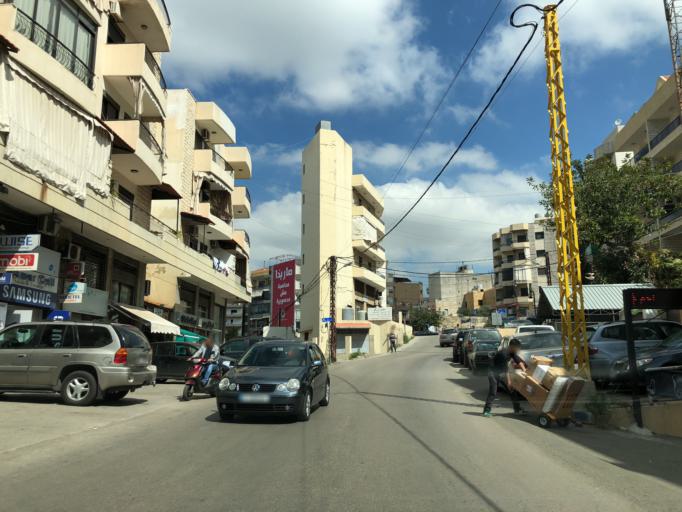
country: LB
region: Mont-Liban
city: Jdaidet el Matn
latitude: 33.8553
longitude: 35.5747
